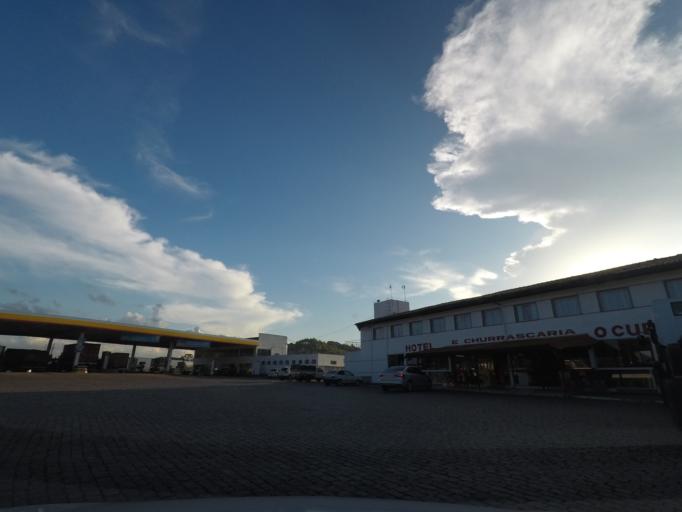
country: BR
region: Parana
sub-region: Campina Grande Do Sul
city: Campina Grande do Sul
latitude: -25.3163
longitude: -49.0162
